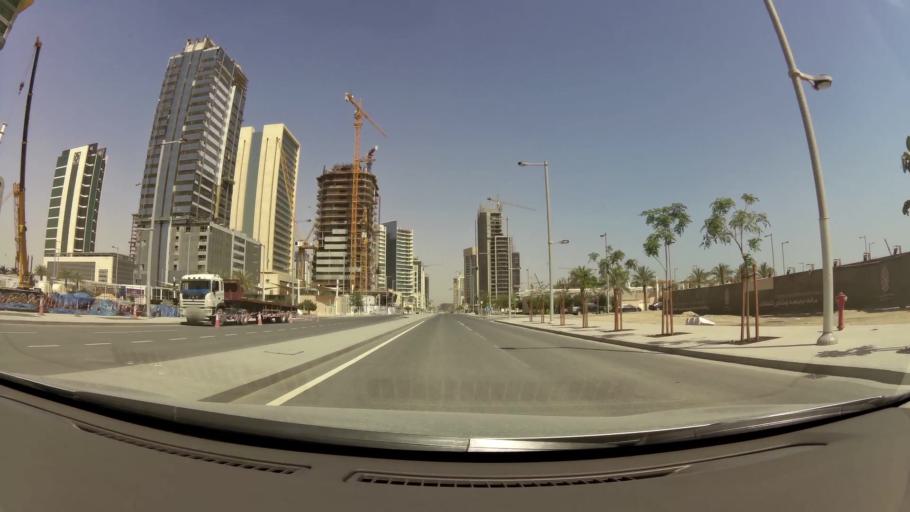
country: QA
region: Baladiyat ad Dawhah
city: Doha
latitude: 25.3875
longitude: 51.5245
